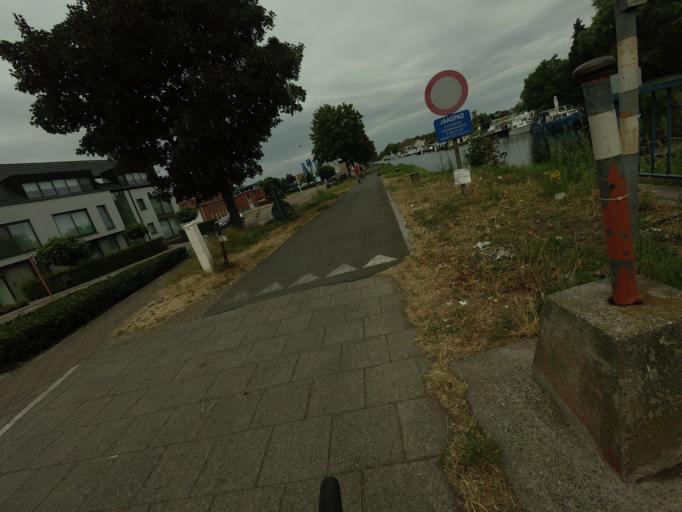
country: BE
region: Flanders
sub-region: Provincie Antwerpen
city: Schoten
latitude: 51.2526
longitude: 4.5072
